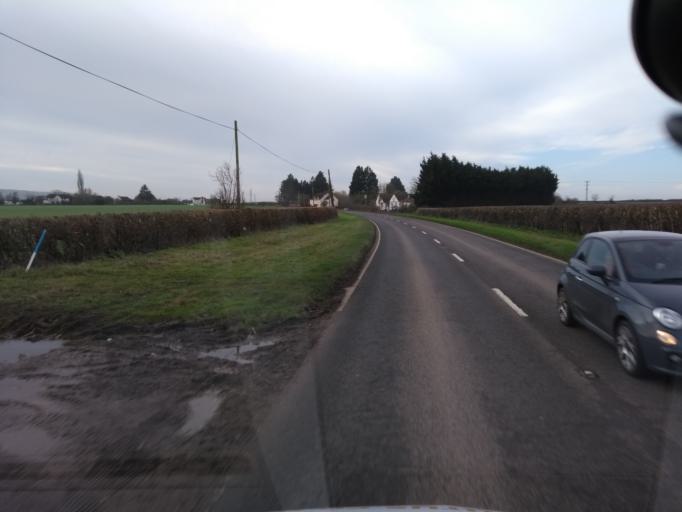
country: GB
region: England
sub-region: Somerset
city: Westonzoyland
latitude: 51.1187
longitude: -2.8510
